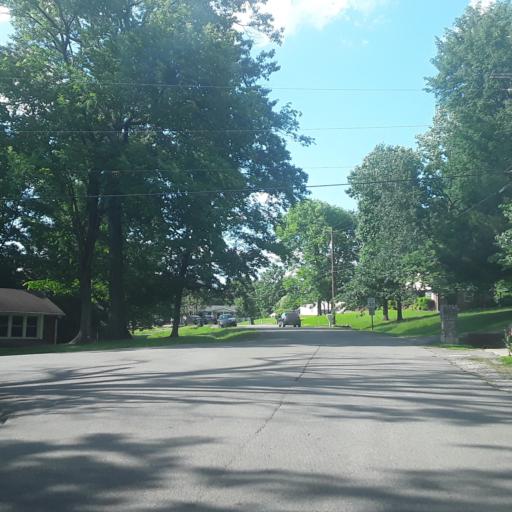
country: US
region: Tennessee
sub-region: Davidson County
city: Lakewood
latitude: 36.2020
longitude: -86.6301
